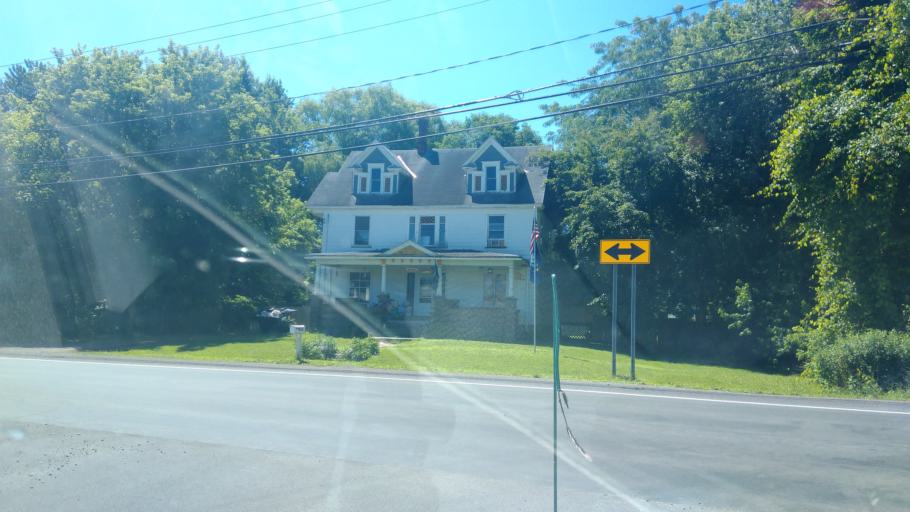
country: US
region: New York
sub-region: Wayne County
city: Sodus
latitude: 43.2113
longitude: -76.9820
